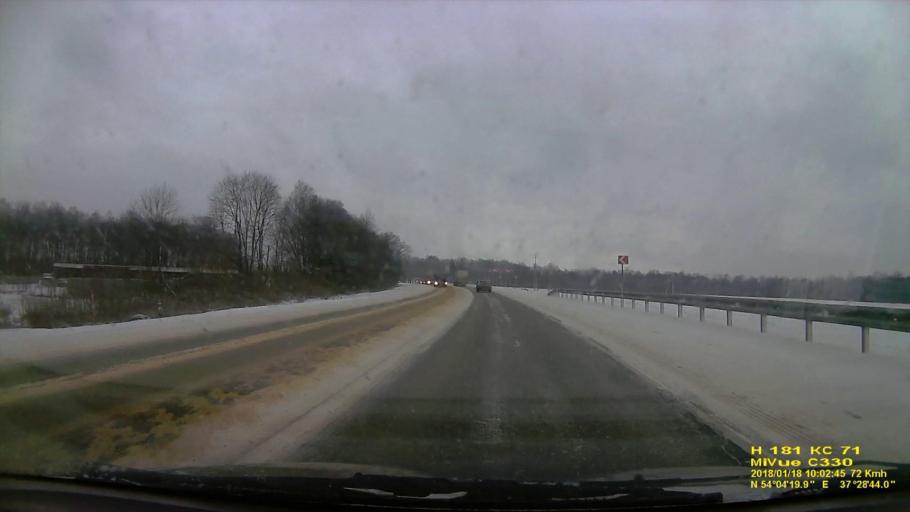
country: RU
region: Tula
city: Pervomayskiy
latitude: 54.0720
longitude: 37.4788
